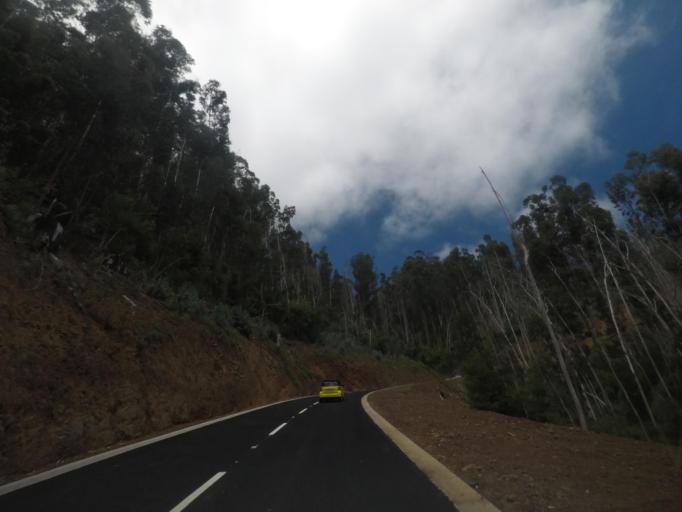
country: PT
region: Madeira
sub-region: Calheta
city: Estreito da Calheta
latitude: 32.7471
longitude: -17.1576
